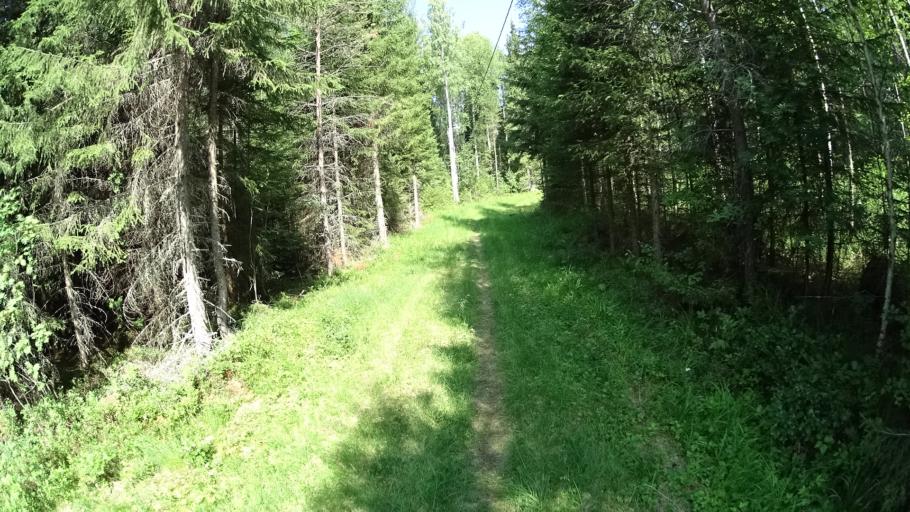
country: FI
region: North Karelia
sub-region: Pielisen Karjala
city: Lieksa
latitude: 63.1225
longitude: 29.8055
